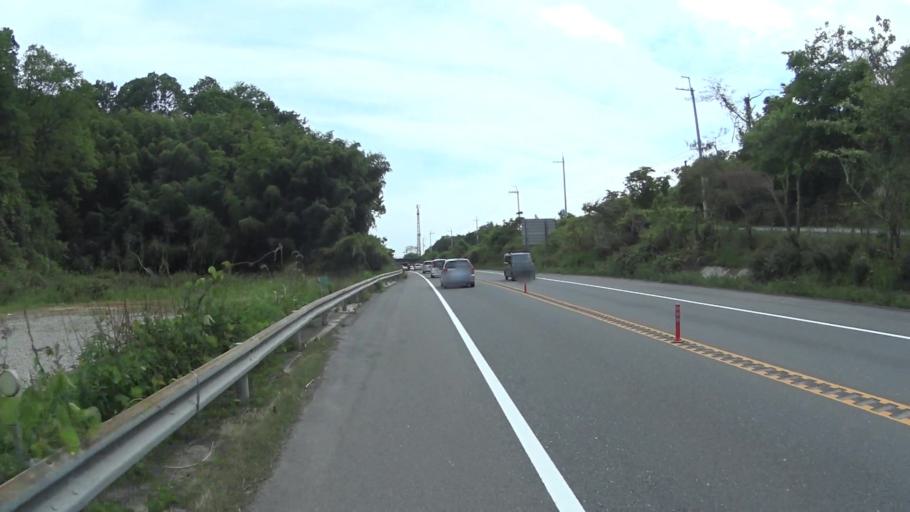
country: JP
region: Shiga Prefecture
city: Kitahama
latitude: 35.1275
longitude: 135.9009
